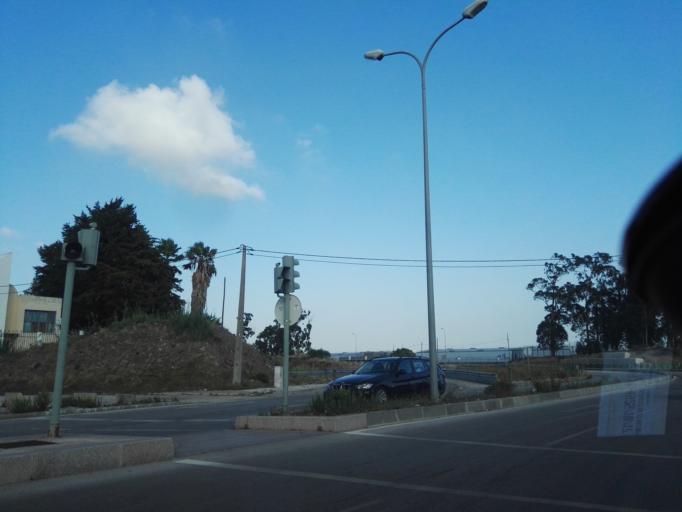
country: PT
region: Lisbon
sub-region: Odivelas
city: Olival do Basto
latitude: 38.7691
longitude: -9.1485
